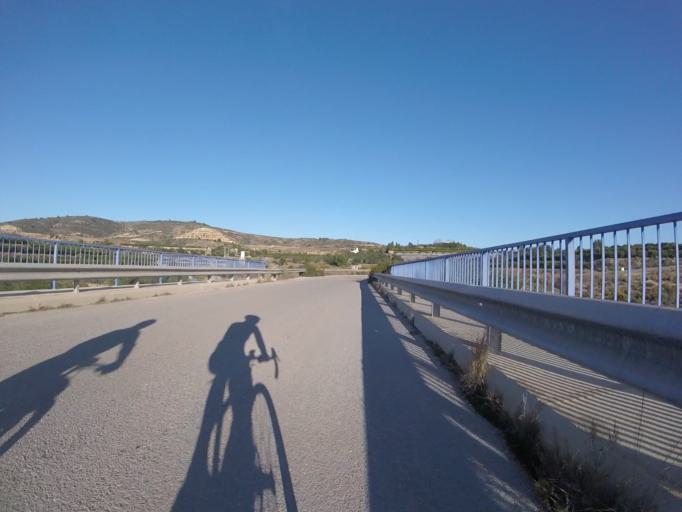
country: ES
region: Valencia
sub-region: Provincia de Castello
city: Torreblanca
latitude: 40.2264
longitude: 0.1982
